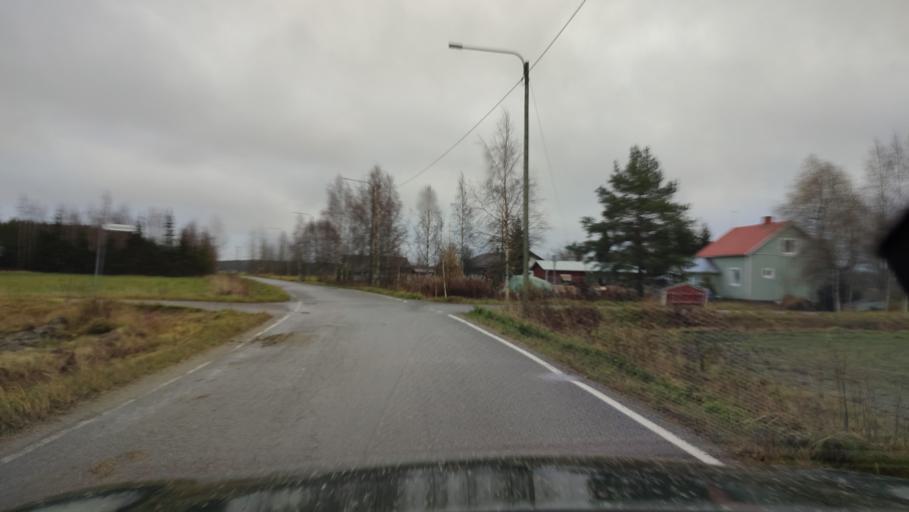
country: FI
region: Southern Ostrobothnia
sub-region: Suupohja
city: Teuva
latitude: 62.4481
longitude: 21.6092
